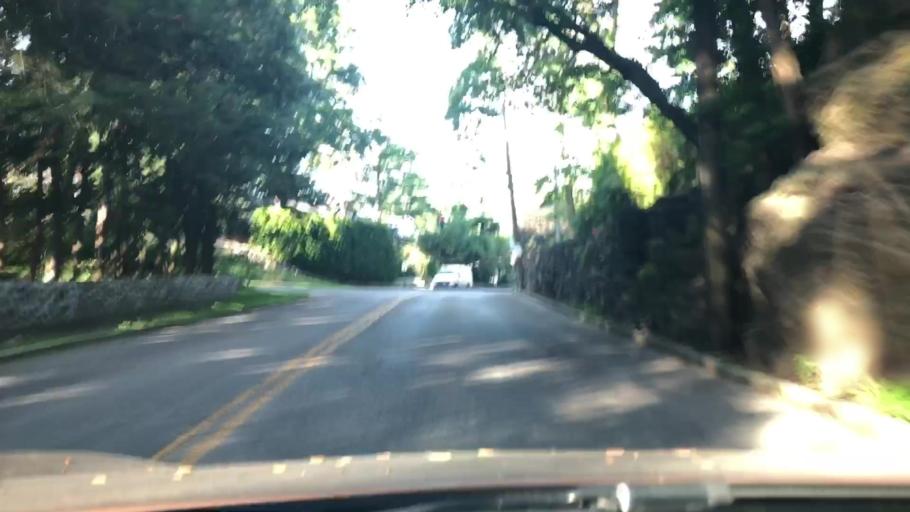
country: US
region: New York
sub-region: Westchester County
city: Bronxville
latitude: 40.9347
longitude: -73.8249
